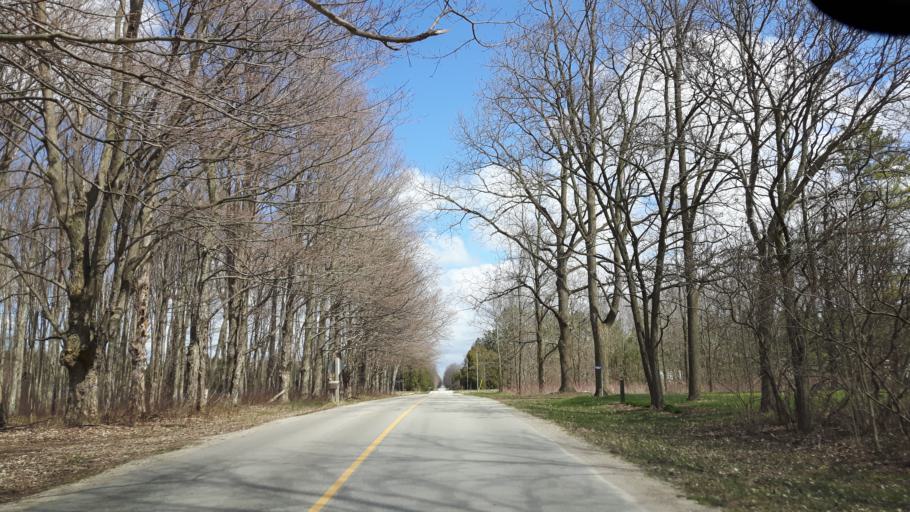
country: CA
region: Ontario
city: Goderich
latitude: 43.6081
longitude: -81.6846
